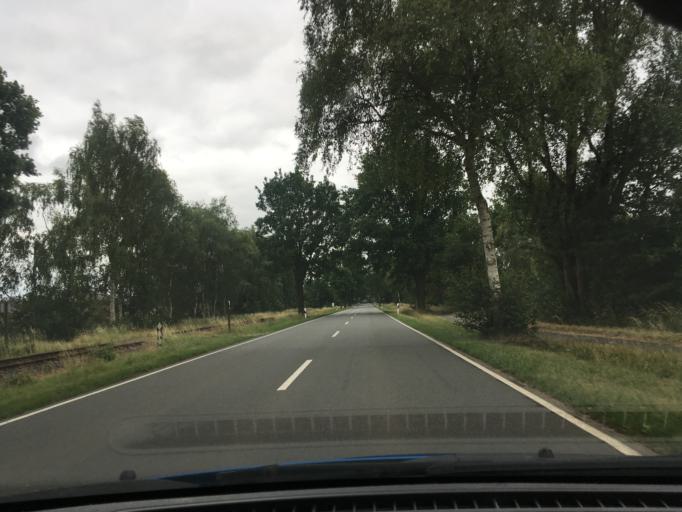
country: DE
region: Lower Saxony
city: Toppenstedt
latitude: 53.2703
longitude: 10.1208
